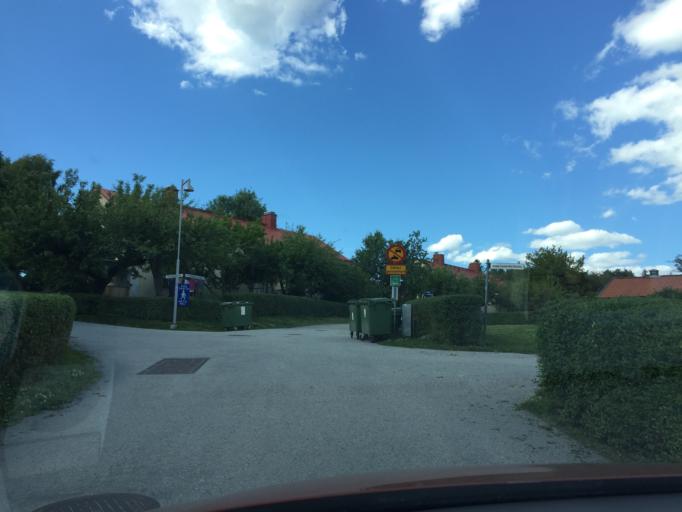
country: SE
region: Stockholm
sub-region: Botkyrka Kommun
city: Tumba
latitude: 59.2020
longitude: 17.8211
